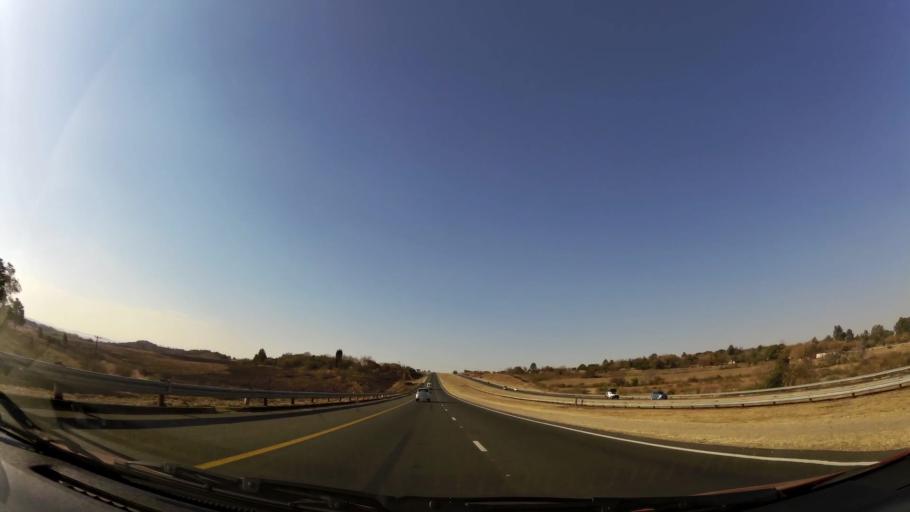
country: ZA
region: Gauteng
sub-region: West Rand District Municipality
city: Muldersdriseloop
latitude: -25.9994
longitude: 27.9046
